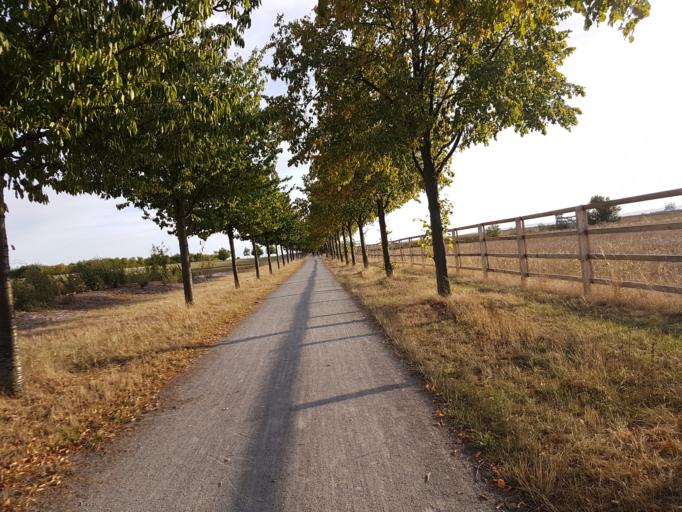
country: DE
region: Lower Saxony
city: Laatzen
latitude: 52.3285
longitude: 9.8317
